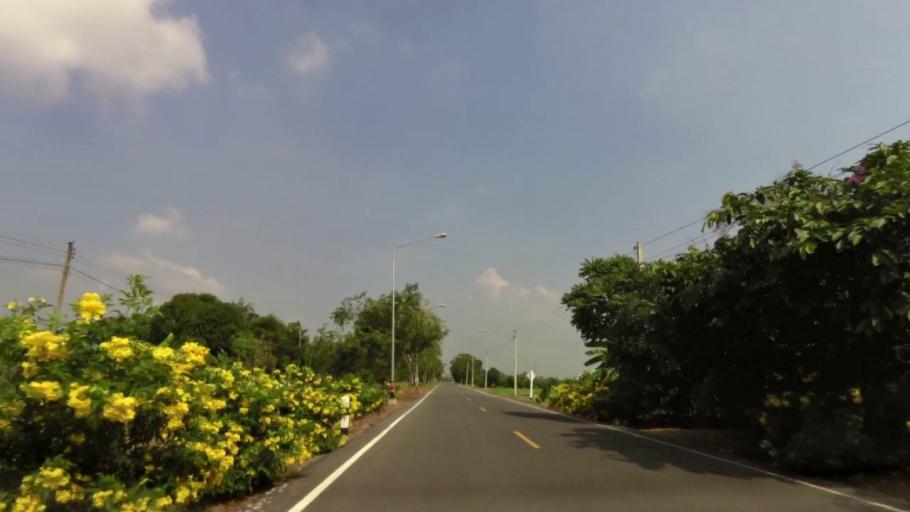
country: TH
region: Ang Thong
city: Wiset Chaichan
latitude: 14.6092
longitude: 100.3954
